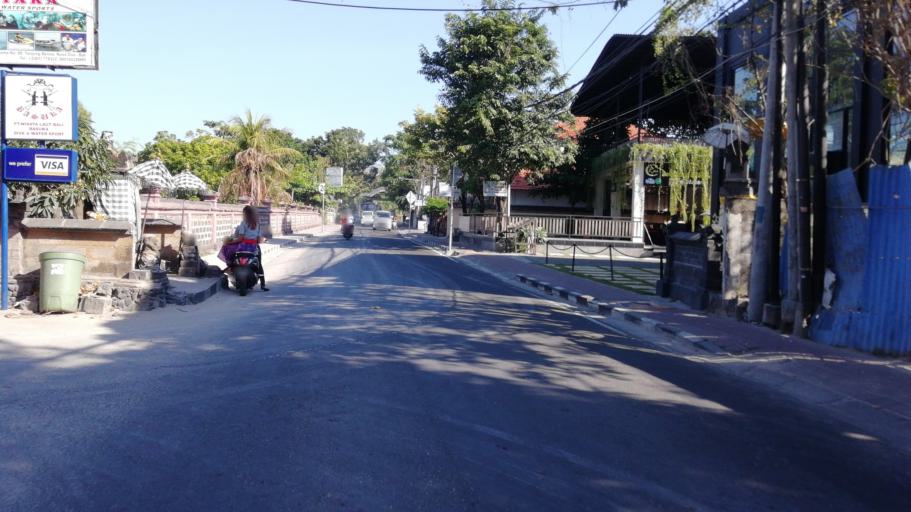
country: ID
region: Bali
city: Bualu
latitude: -8.7617
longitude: 115.2220
